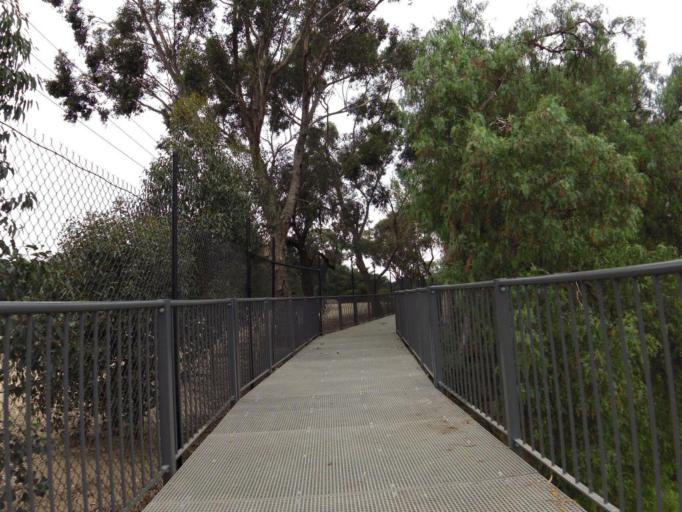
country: AU
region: Victoria
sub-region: Moorabool
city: Bacchus Marsh
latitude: -37.6598
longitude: 144.4501
